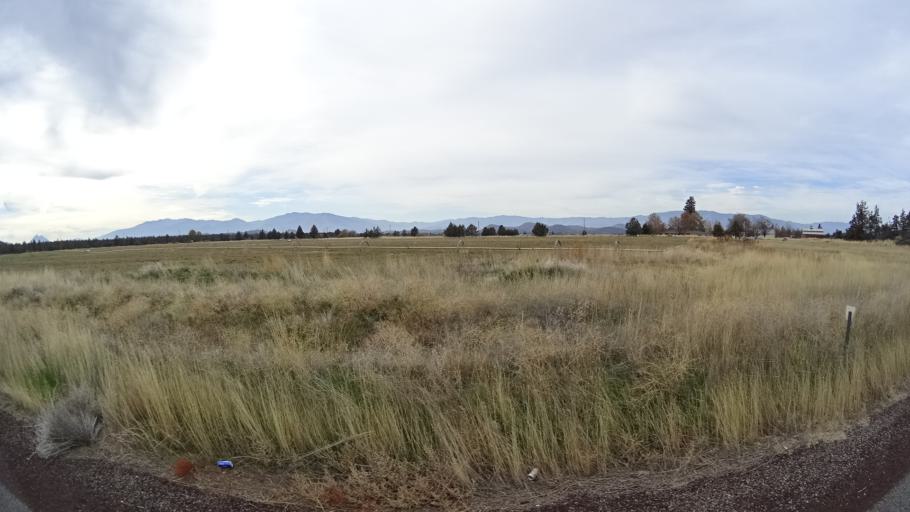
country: US
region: California
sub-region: Siskiyou County
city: Montague
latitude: 41.6225
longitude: -122.3775
